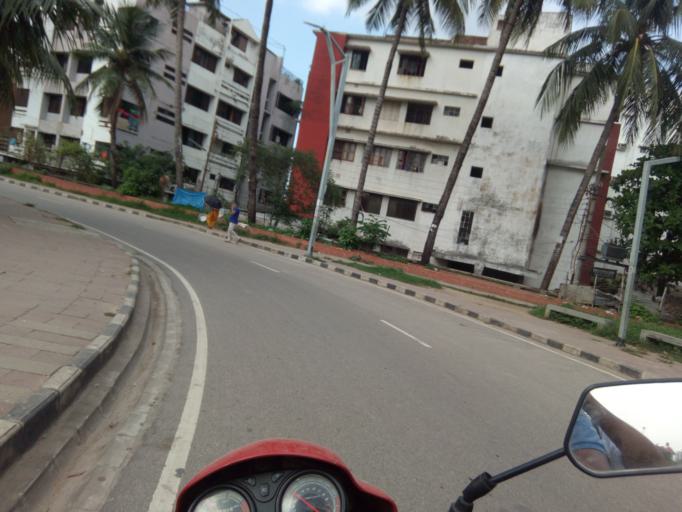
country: BD
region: Dhaka
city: Paltan
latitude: 23.7508
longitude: 90.3992
